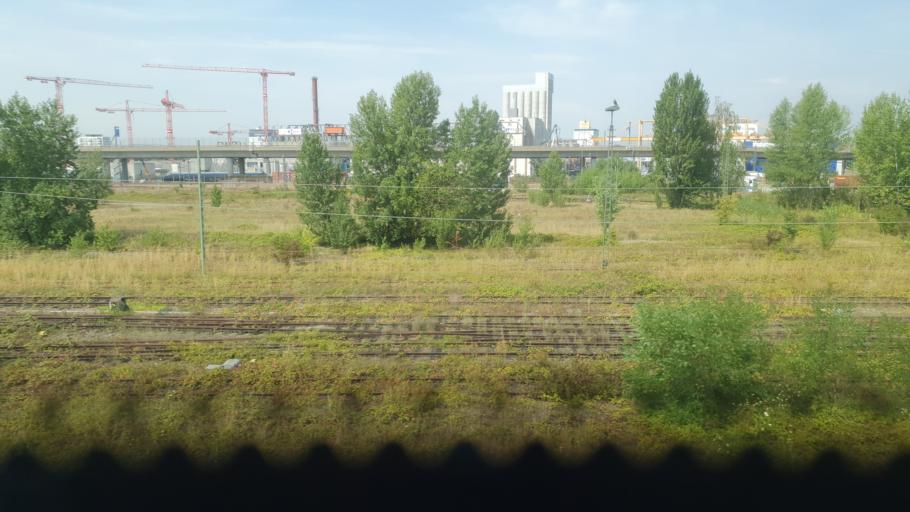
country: DE
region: Baden-Wuerttemberg
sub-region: Freiburg Region
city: Weil am Rhein
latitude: 47.5840
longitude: 7.6047
